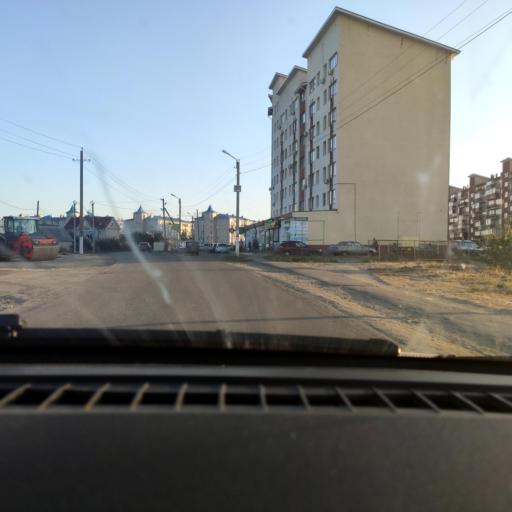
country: RU
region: Voronezj
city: Novaya Usman'
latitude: 51.6085
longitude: 39.3875
